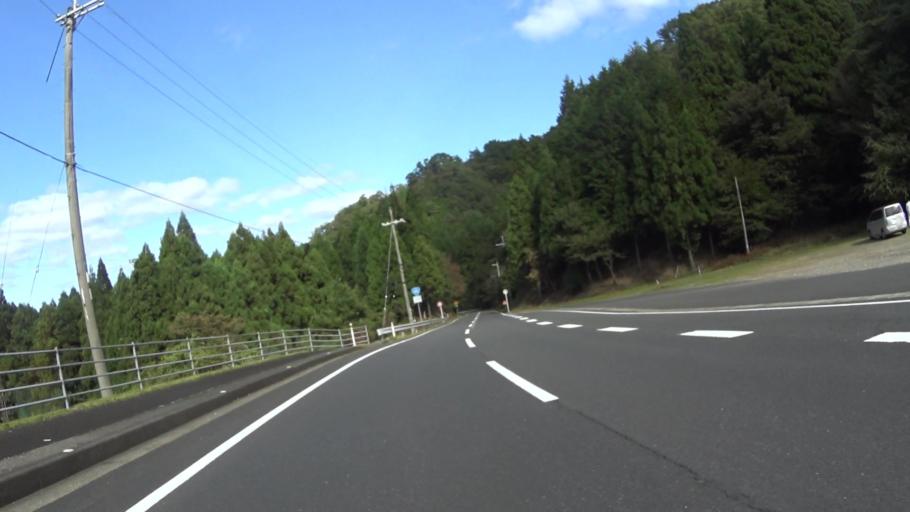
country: JP
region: Hyogo
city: Toyooka
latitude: 35.5341
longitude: 134.9779
